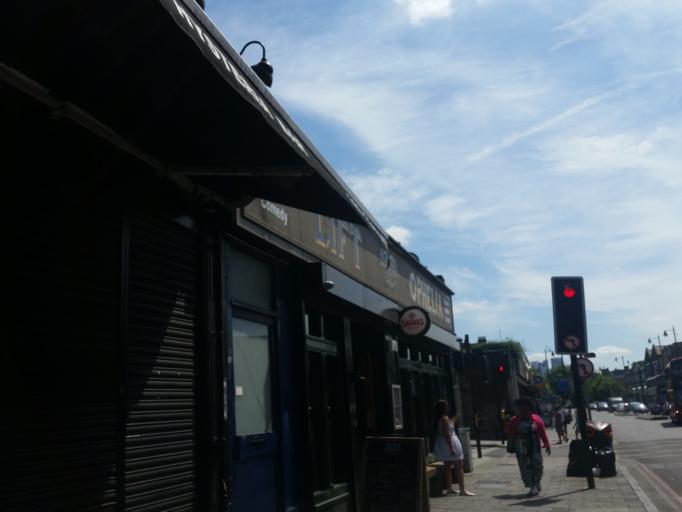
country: GB
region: England
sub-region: Greater London
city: Bethnal Green
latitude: 51.5456
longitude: -0.0758
